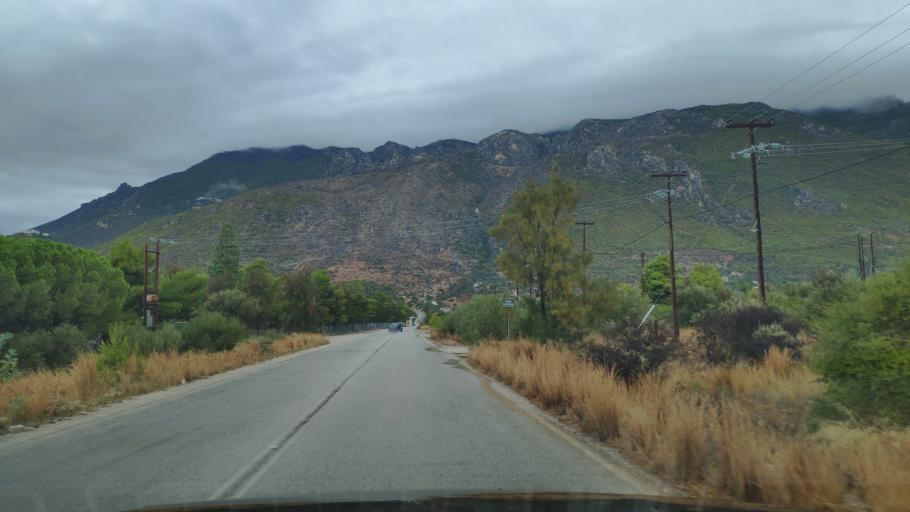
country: GR
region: Peloponnese
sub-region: Nomos Korinthias
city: Loutraki
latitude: 37.9702
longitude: 22.9875
